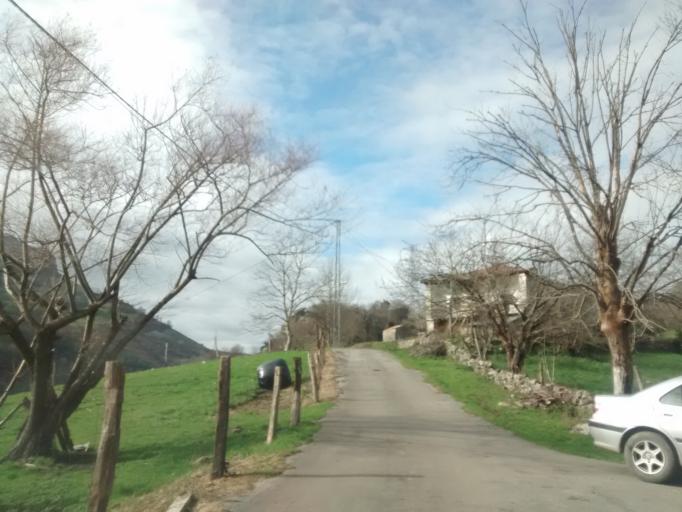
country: ES
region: Cantabria
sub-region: Provincia de Cantabria
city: Lierganes
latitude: 43.3218
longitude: -3.7162
